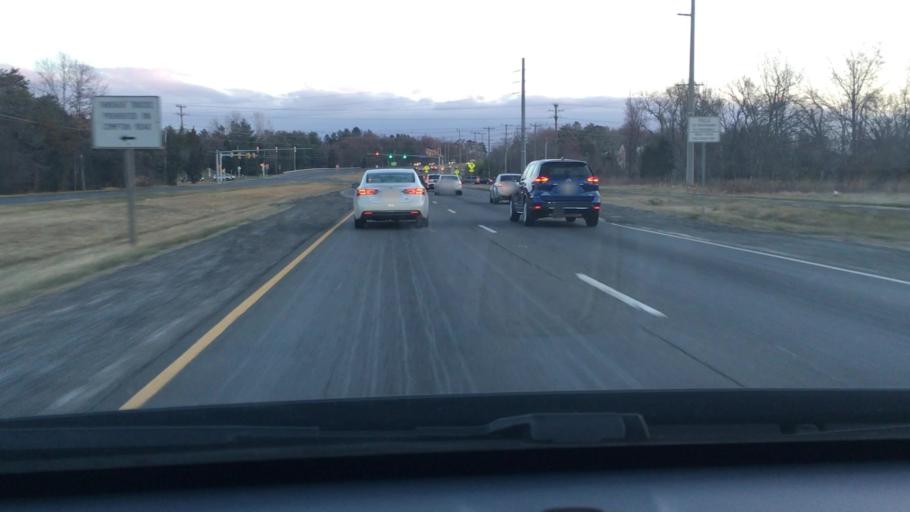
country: US
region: Virginia
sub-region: Prince William County
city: Yorkshire
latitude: 38.8080
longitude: -77.4491
